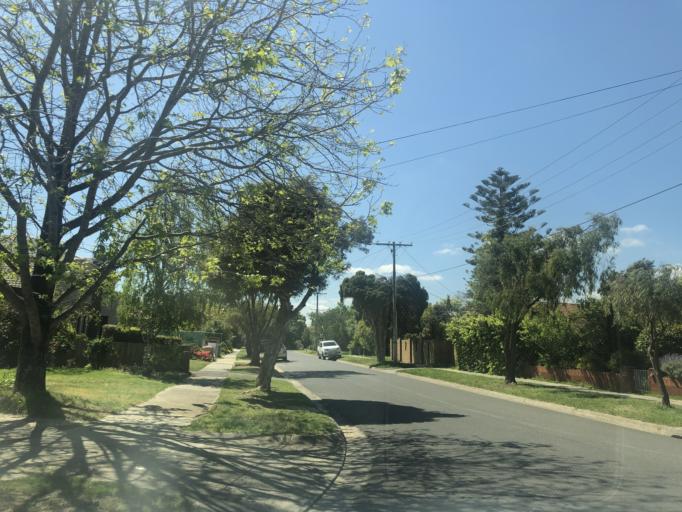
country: AU
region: Victoria
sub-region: Monash
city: Notting Hill
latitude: -37.9031
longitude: 145.1664
